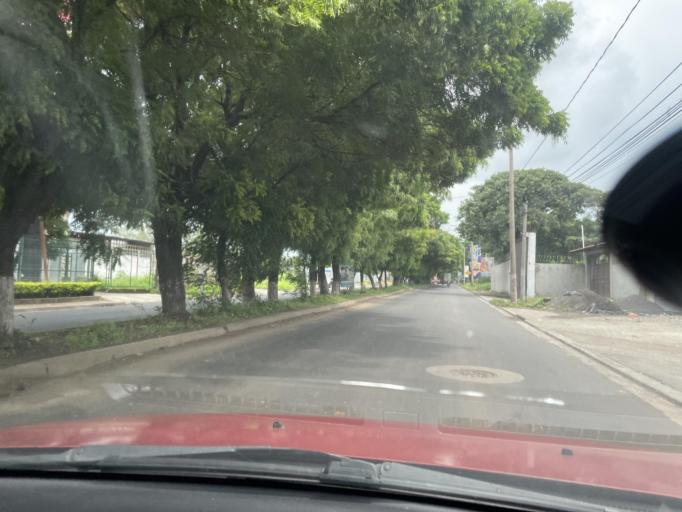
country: SV
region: San Miguel
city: San Miguel
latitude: 13.4500
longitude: -88.1582
